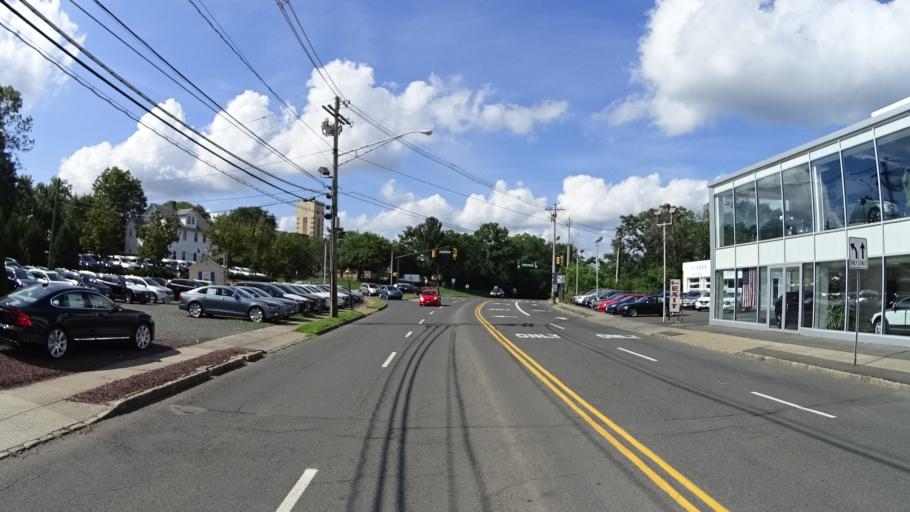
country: US
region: New Jersey
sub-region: Morris County
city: Chatham
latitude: 40.7301
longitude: -74.3761
